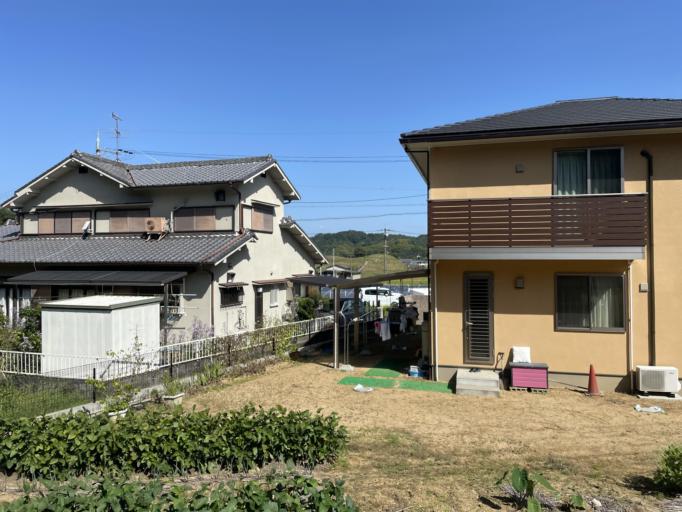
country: JP
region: Nara
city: Gose
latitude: 34.4416
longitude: 135.7745
